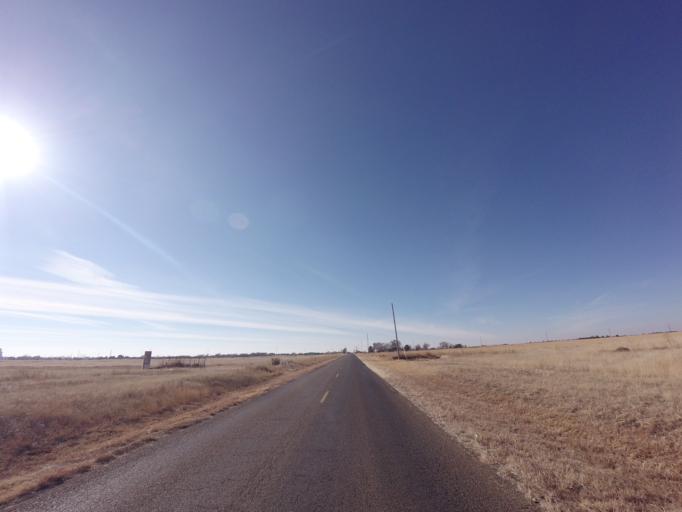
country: US
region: New Mexico
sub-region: Curry County
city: Clovis
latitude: 34.4192
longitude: -103.2400
